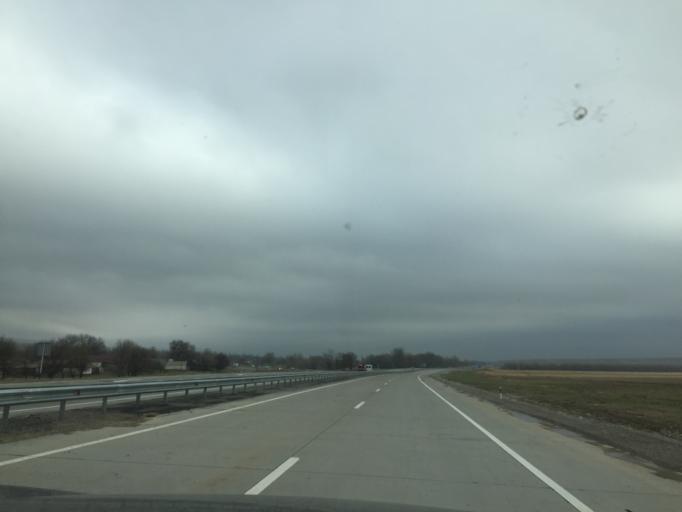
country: KZ
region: Ongtustik Qazaqstan
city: Kokterek
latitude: 42.5546
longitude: 70.1433
